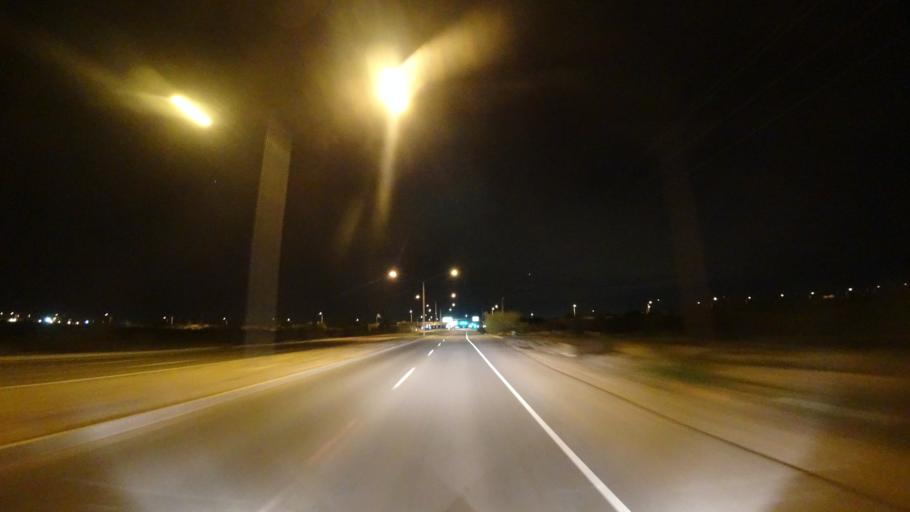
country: US
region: Arizona
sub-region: Maricopa County
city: Queen Creek
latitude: 33.3503
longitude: -111.6399
